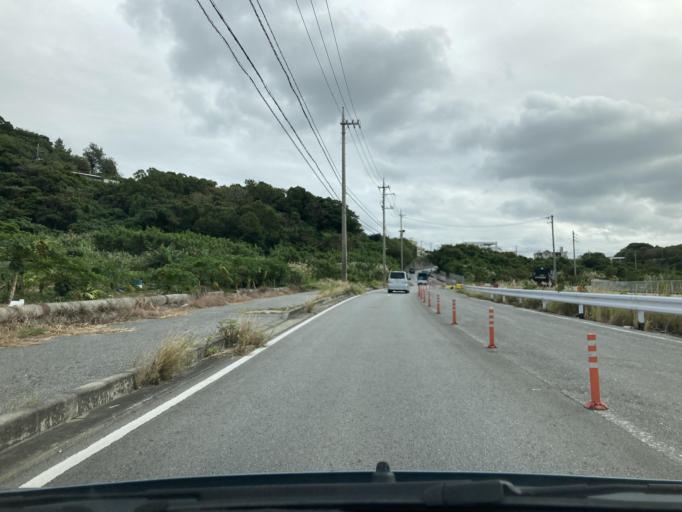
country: JP
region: Okinawa
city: Tomigusuku
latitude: 26.1650
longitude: 127.6788
